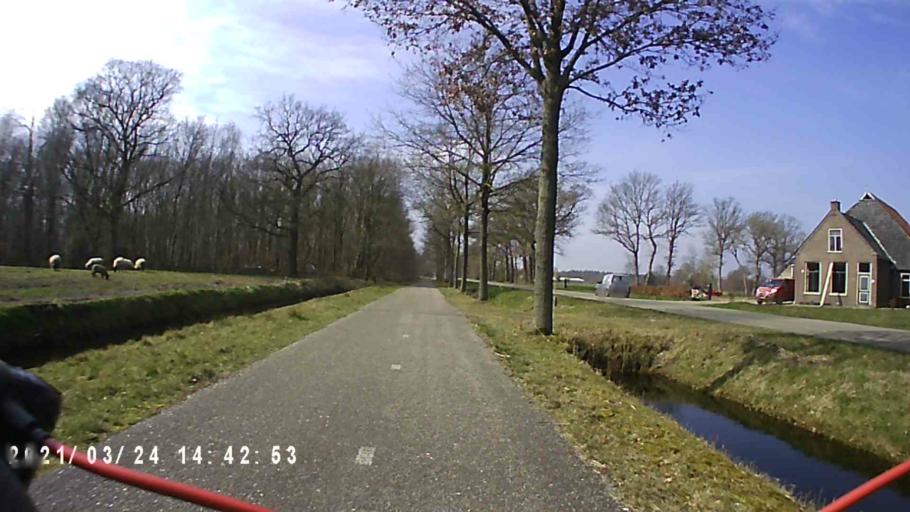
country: NL
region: Friesland
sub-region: Gemeente Heerenveen
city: Jubbega
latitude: 53.0319
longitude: 6.1276
